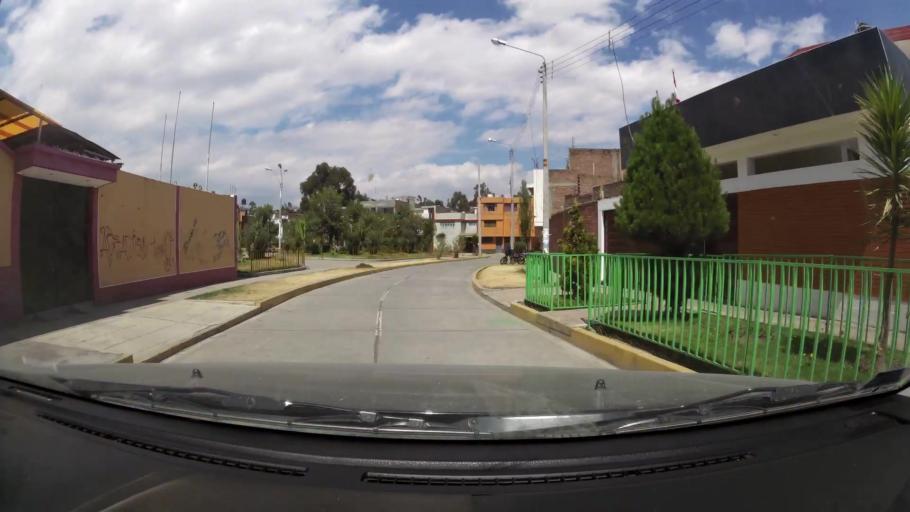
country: PE
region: Junin
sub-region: Provincia de Huancayo
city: El Tambo
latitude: -12.0665
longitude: -75.2195
